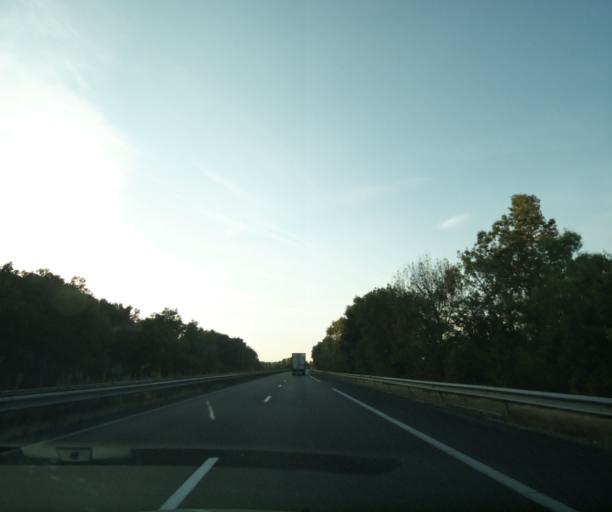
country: FR
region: Aquitaine
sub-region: Departement du Lot-et-Garonne
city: Layrac
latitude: 44.1305
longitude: 0.6833
